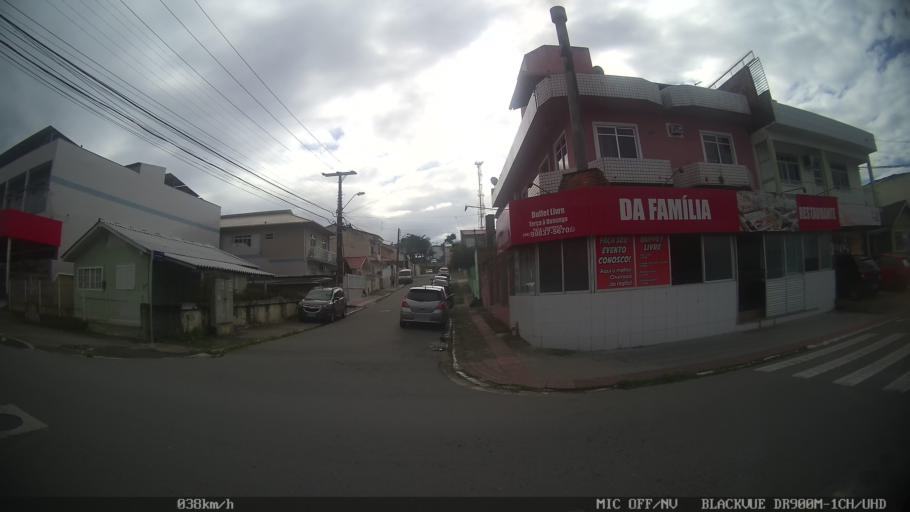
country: BR
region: Santa Catarina
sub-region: Sao Jose
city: Campinas
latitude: -27.5696
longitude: -48.6160
